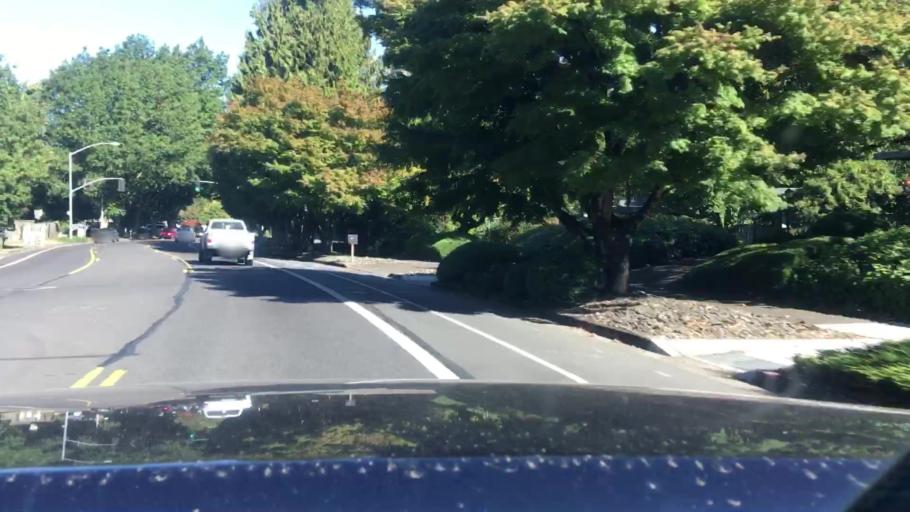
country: US
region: Oregon
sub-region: Lane County
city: Eugene
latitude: 44.0693
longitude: -123.0651
